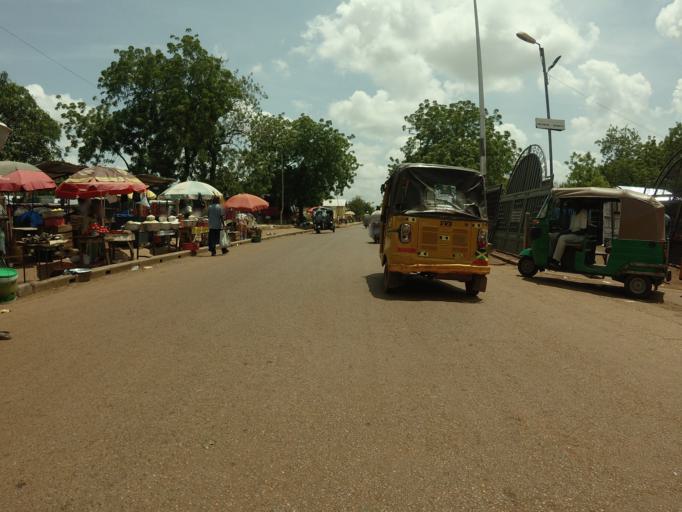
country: GH
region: Northern
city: Tamale
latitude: 9.4014
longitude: -0.8484
